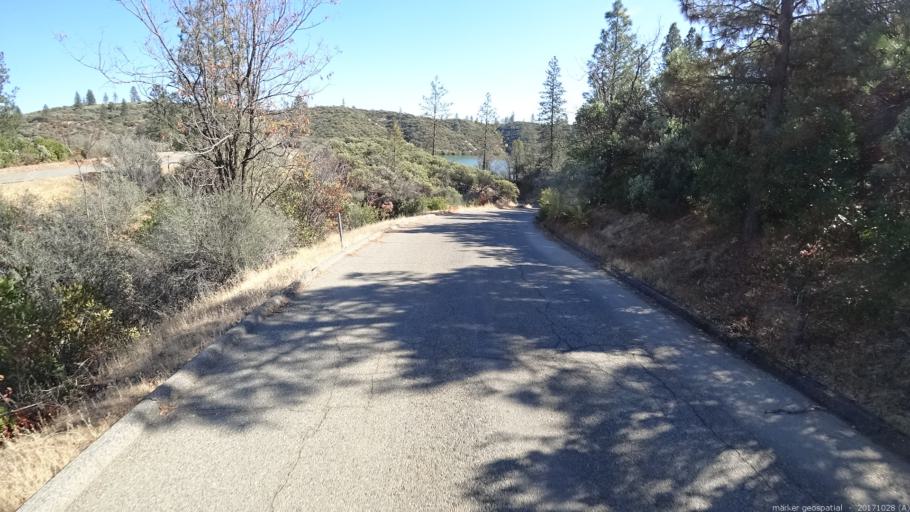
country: US
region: California
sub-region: Shasta County
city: Shasta
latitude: 40.6323
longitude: -122.4533
